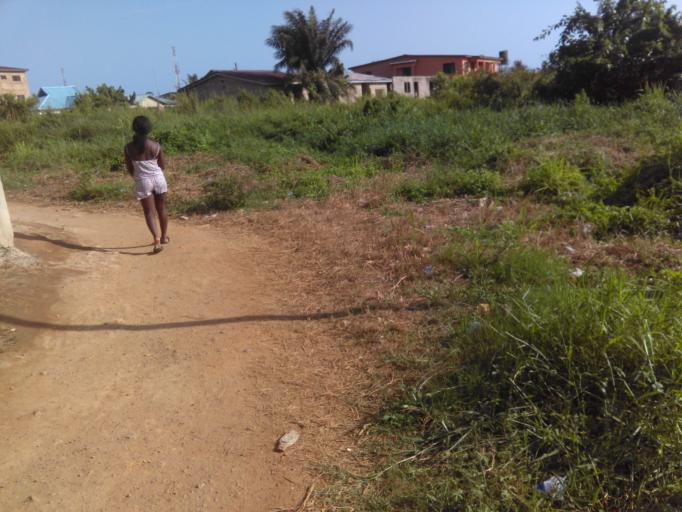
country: GH
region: Central
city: Cape Coast
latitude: 5.1133
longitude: -1.2980
